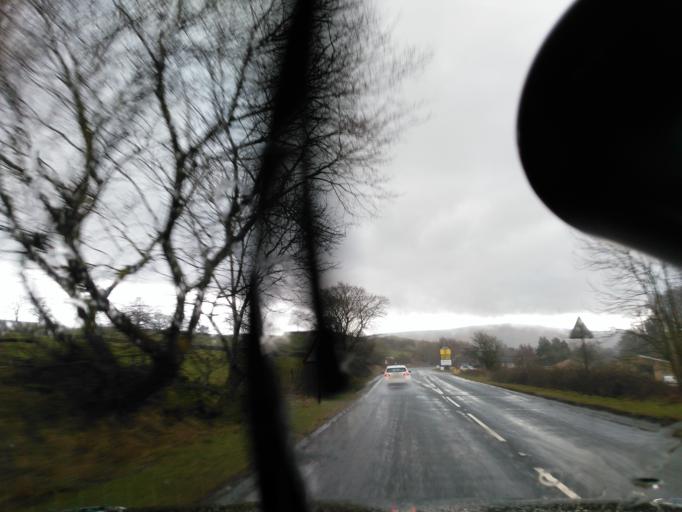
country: GB
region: England
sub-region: Bradford
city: Addingham
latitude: 53.9782
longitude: -1.9144
